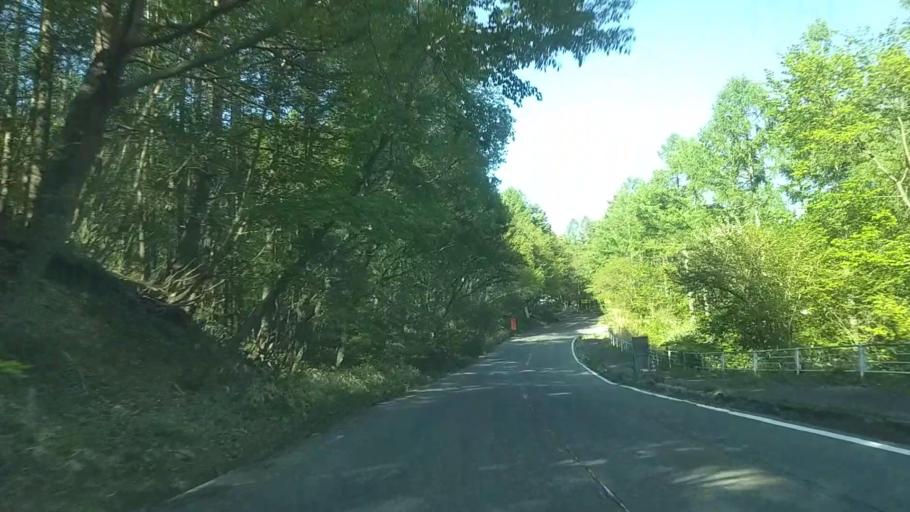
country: JP
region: Yamanashi
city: Nirasaki
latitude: 35.9002
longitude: 138.3728
